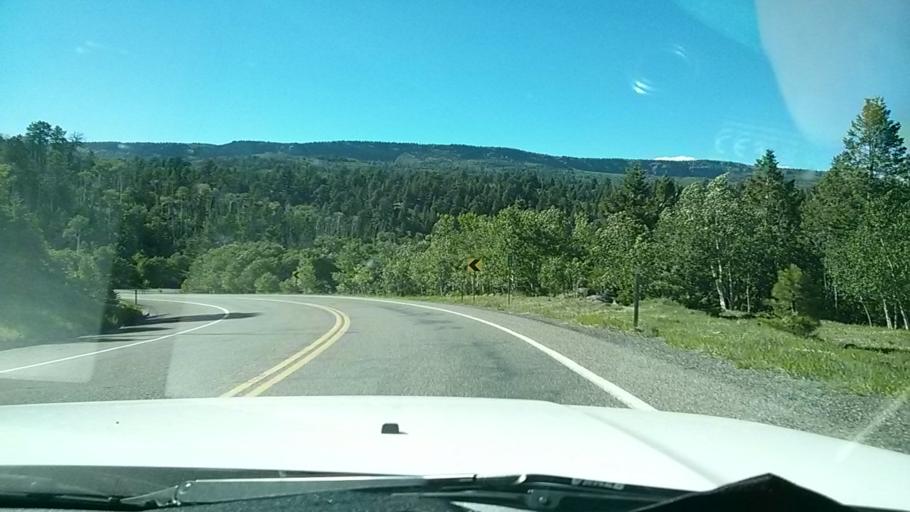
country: US
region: Utah
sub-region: Wayne County
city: Loa
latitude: 38.0906
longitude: -111.3439
